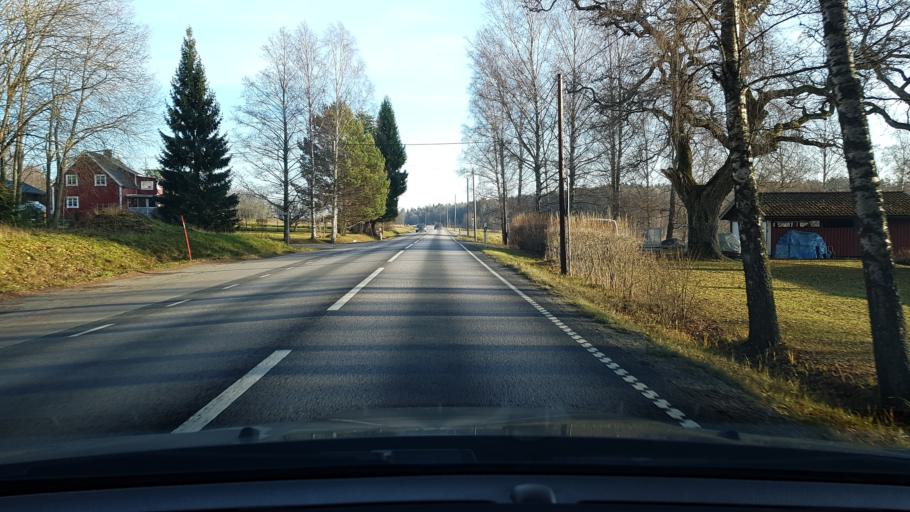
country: SE
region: Stockholm
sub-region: Norrtalje Kommun
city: Nykvarn
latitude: 59.7353
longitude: 18.2714
